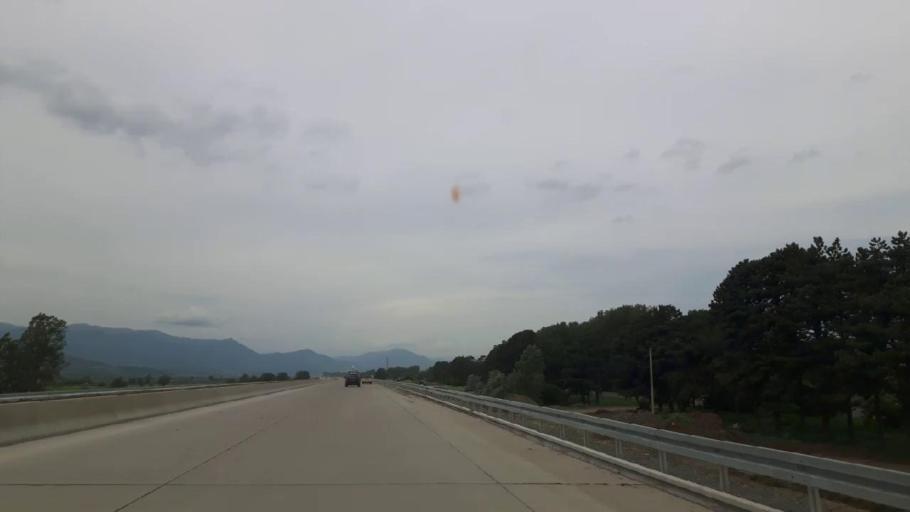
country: GE
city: Agara
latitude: 42.0190
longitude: 43.7400
